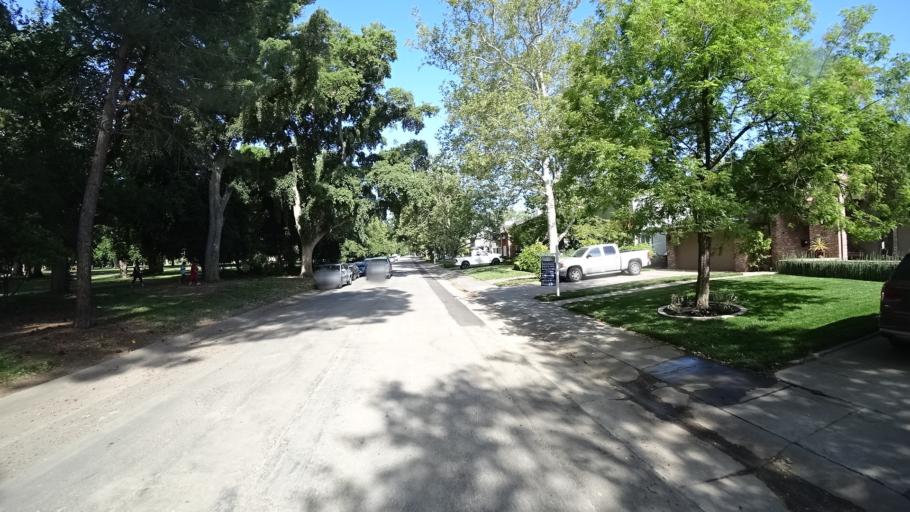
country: US
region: California
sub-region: Sacramento County
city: Sacramento
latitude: 38.5467
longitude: -121.5050
